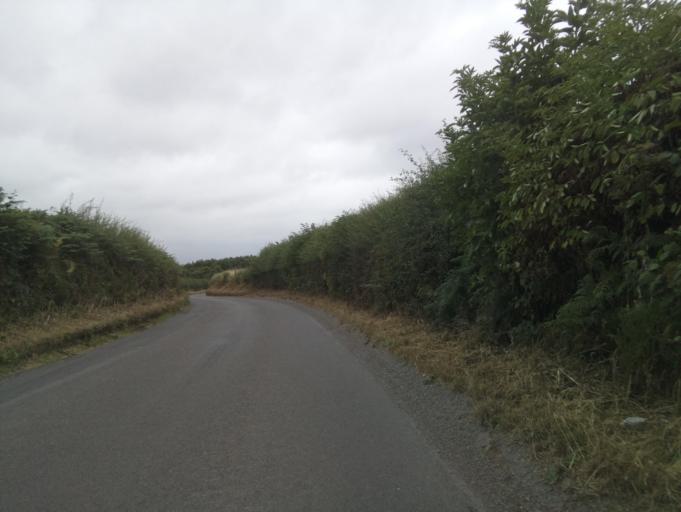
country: GB
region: England
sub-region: Leicestershire
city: Ashby de la Zouch
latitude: 52.7767
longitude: -1.5078
